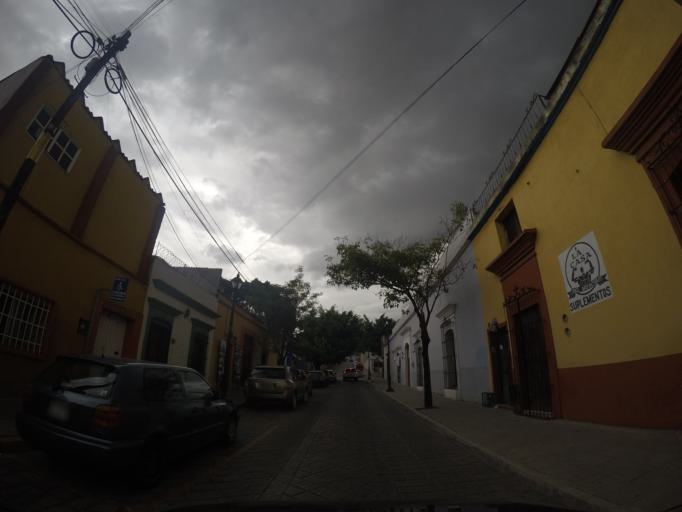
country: MX
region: Oaxaca
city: Oaxaca de Juarez
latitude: 17.0685
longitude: -96.7228
